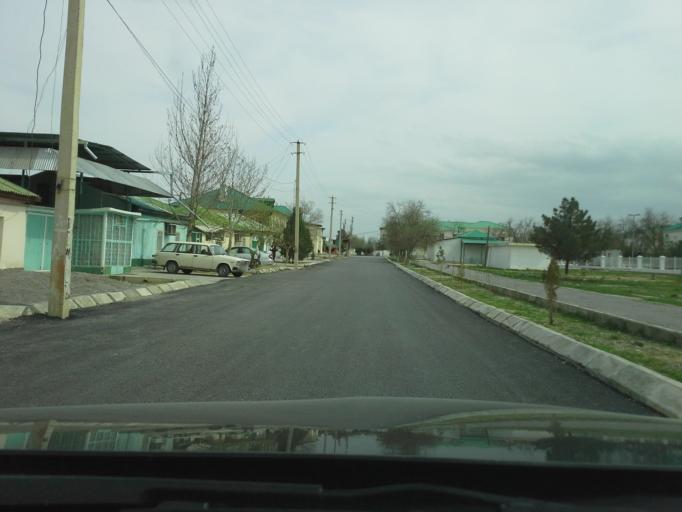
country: TM
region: Ahal
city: Abadan
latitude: 38.0617
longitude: 58.1528
